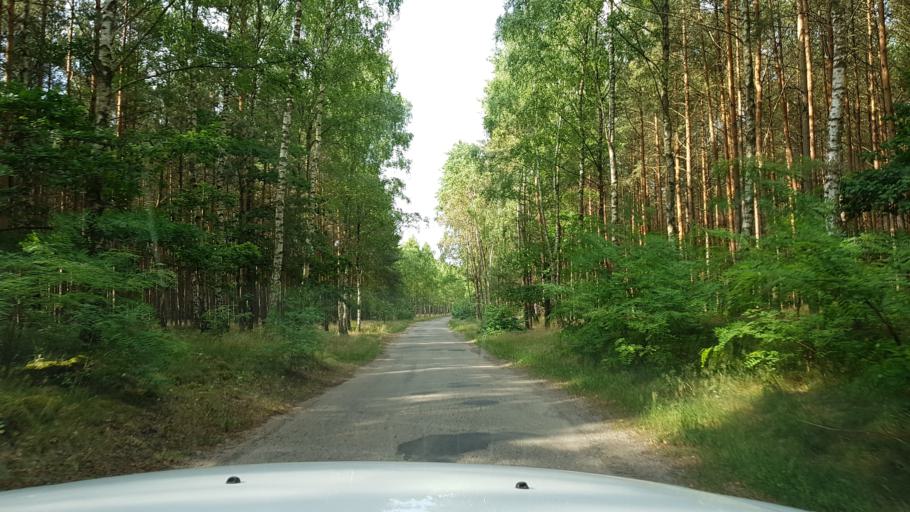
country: PL
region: West Pomeranian Voivodeship
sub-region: Powiat gryfinski
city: Gryfino
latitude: 53.2443
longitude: 14.5604
